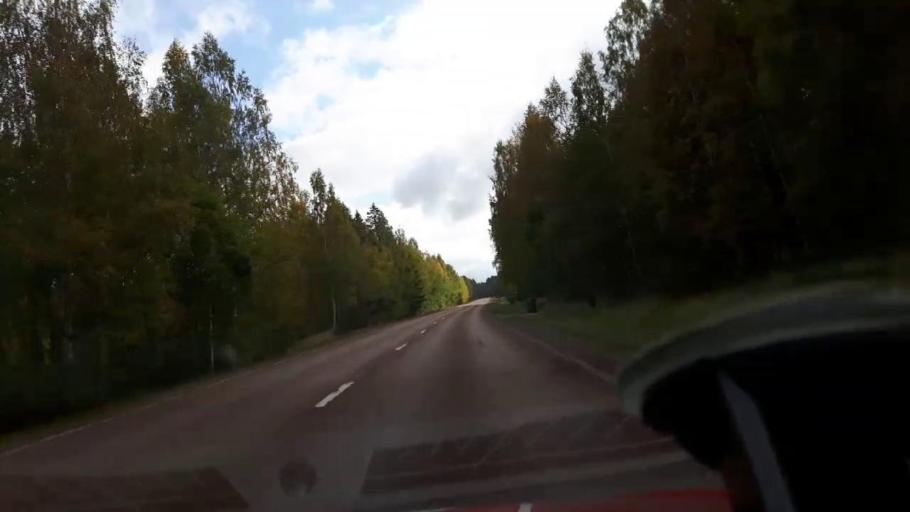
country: SE
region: Gaevleborg
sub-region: Ljusdals Kommun
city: Jaervsoe
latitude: 61.6429
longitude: 16.2254
